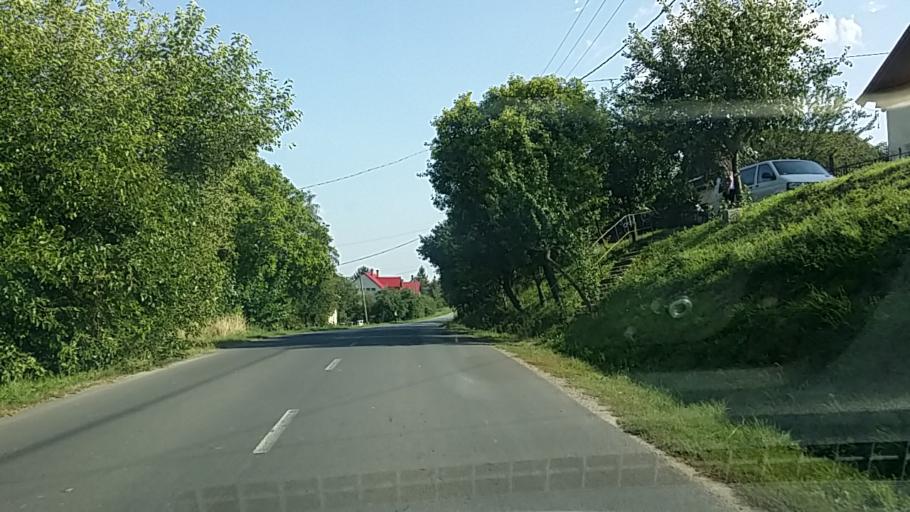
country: HU
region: Nograd
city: Bujak
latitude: 47.8808
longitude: 19.5520
